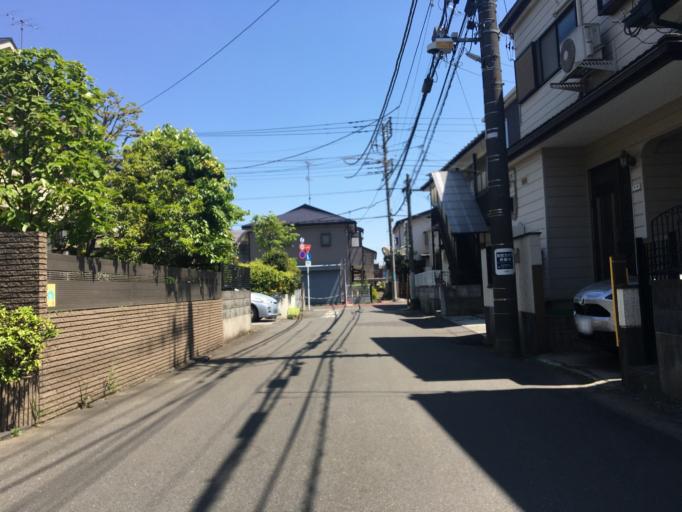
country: JP
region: Tokyo
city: Kokubunji
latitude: 35.7191
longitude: 139.4938
